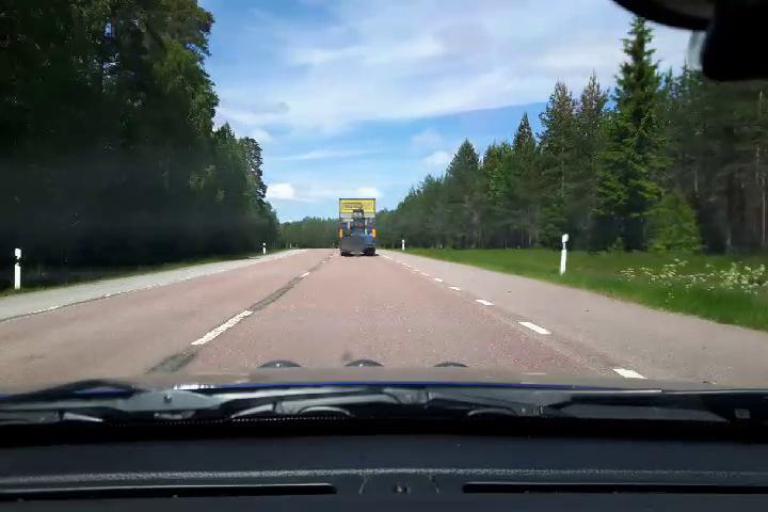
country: SE
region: Uppsala
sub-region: Osthammars Kommun
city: Bjorklinge
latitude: 60.1285
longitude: 17.5096
